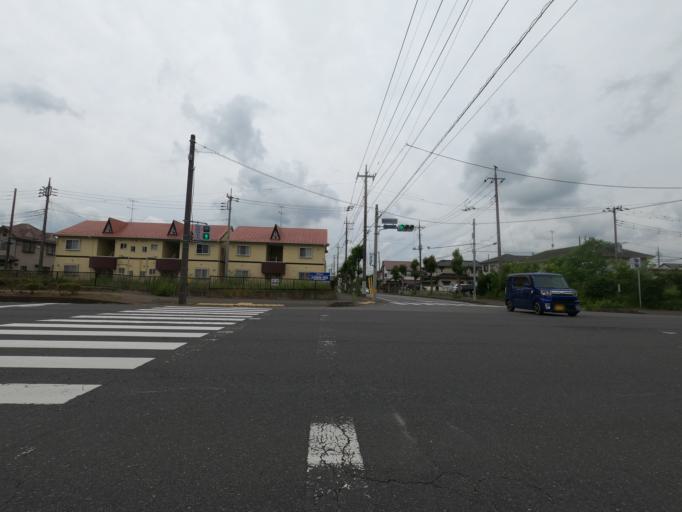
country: JP
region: Ibaraki
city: Moriya
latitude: 35.9669
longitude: 139.9645
